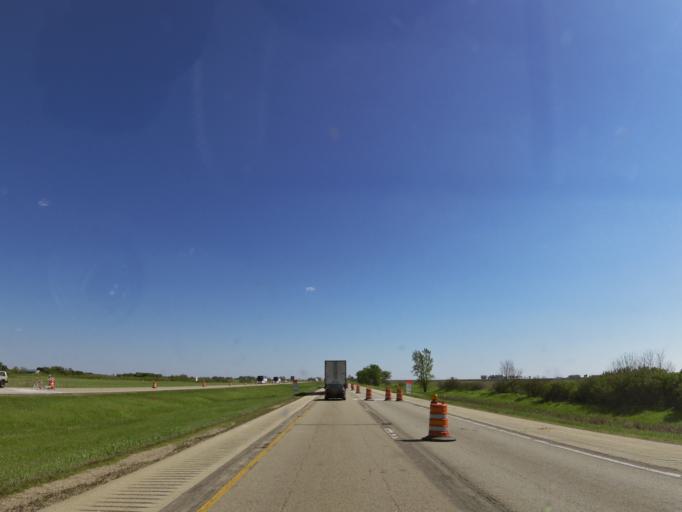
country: US
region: Illinois
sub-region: Ogle County
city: Hillcrest
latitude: 42.0009
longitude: -89.0212
